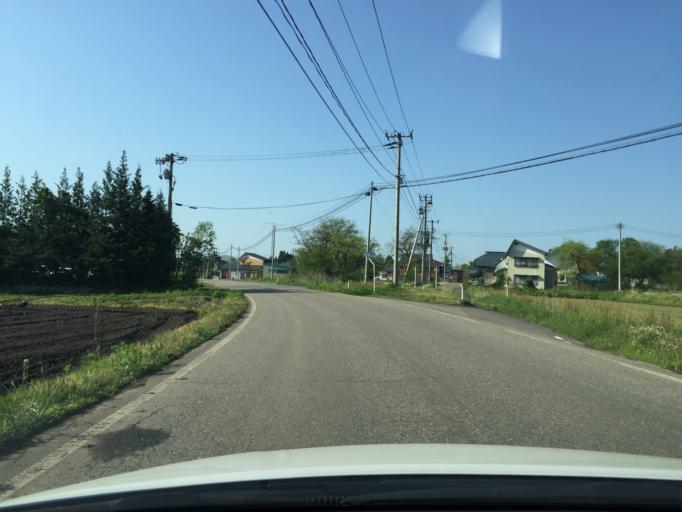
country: JP
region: Fukushima
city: Kitakata
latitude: 37.6556
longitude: 139.7745
